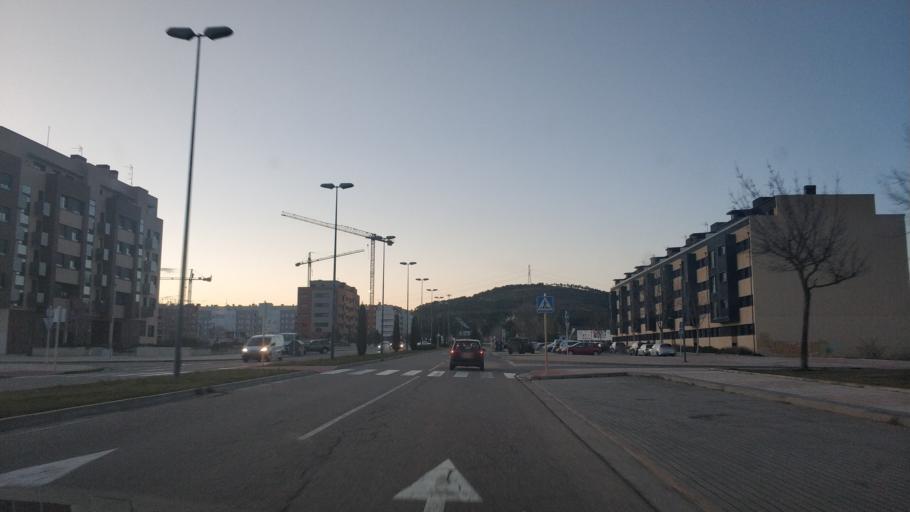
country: ES
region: Castille and Leon
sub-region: Provincia de Burgos
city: Burgos
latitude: 42.3626
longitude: -3.6691
